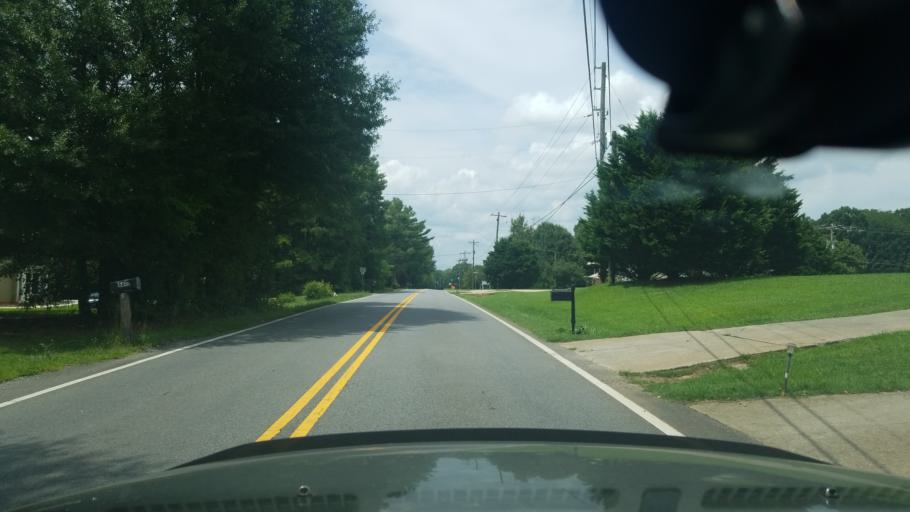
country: US
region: Georgia
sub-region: Forsyth County
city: Cumming
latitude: 34.2686
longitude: -84.2358
